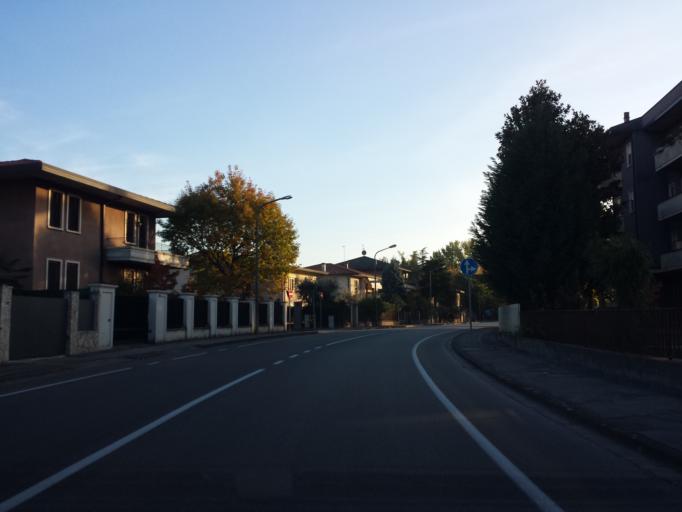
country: IT
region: Veneto
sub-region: Provincia di Vicenza
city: Vicenza
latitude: 45.5761
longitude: 11.5457
